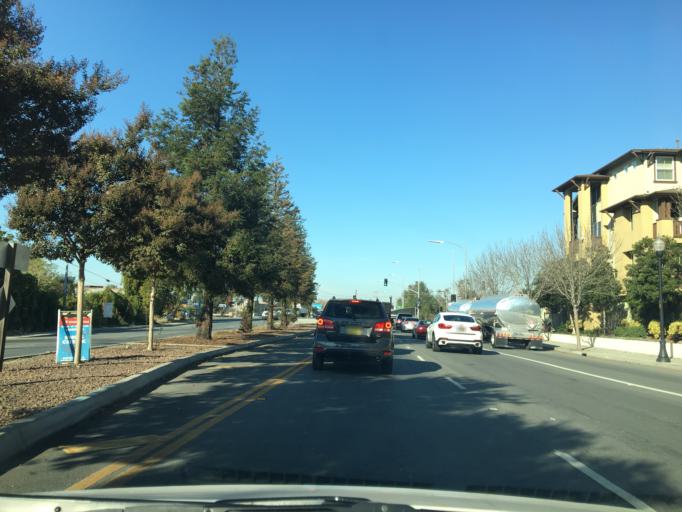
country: US
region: California
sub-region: Santa Clara County
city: San Jose
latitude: 37.3615
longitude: -121.8913
